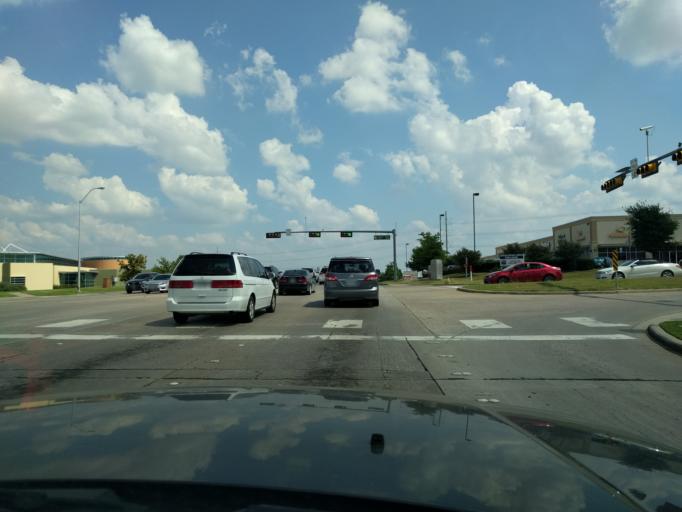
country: US
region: Texas
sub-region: Collin County
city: Allen
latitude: 33.0678
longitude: -96.6989
